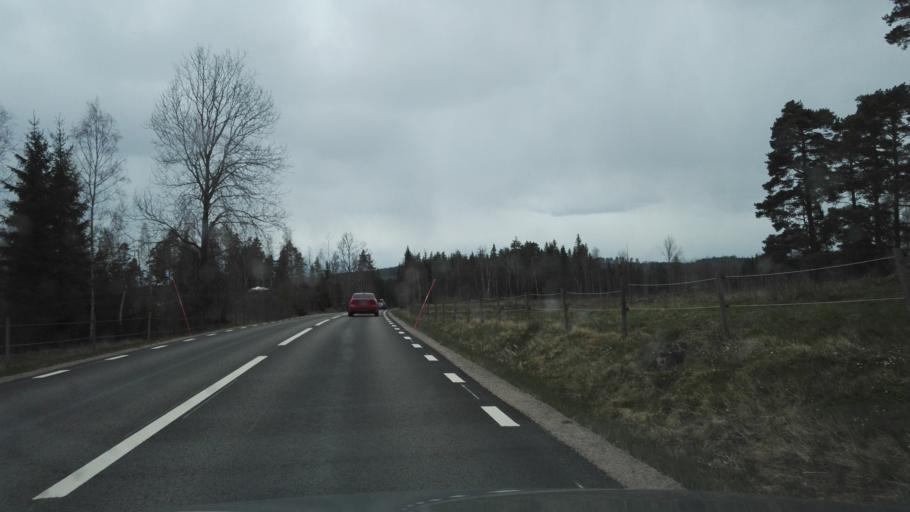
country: SE
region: Kronoberg
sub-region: Vaxjo Kommun
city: Braas
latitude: 57.1395
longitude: 14.9646
